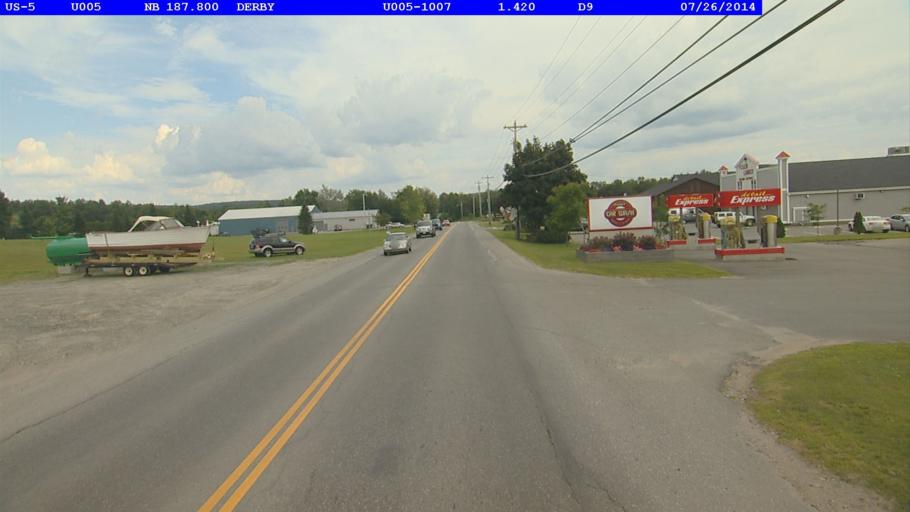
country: US
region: Vermont
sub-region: Orleans County
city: Newport
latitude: 44.9528
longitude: -72.1421
